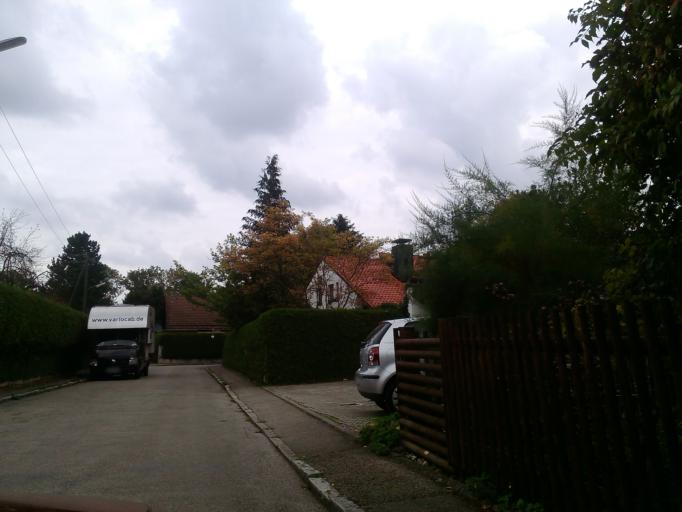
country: DE
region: Bavaria
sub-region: Upper Bavaria
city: Krailling
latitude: 48.0977
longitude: 11.4028
